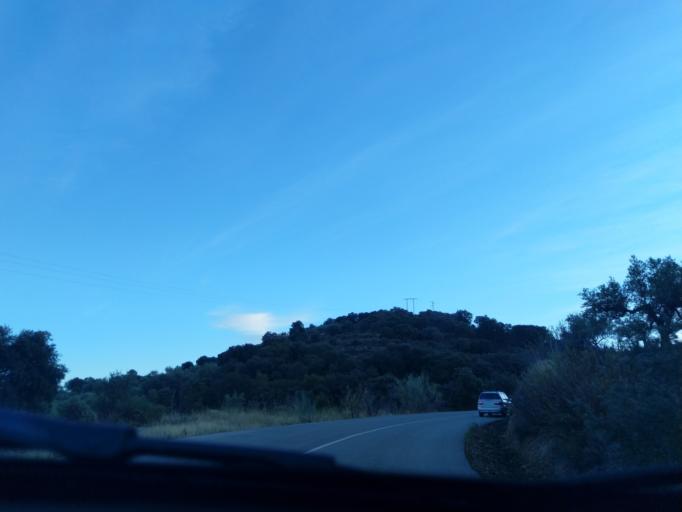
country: ES
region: Extremadura
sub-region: Provincia de Badajoz
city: Reina
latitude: 38.1609
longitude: -5.8995
